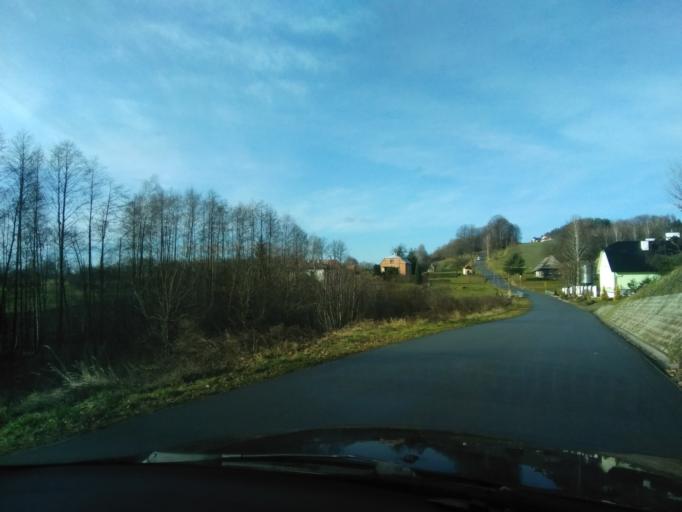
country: PL
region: Subcarpathian Voivodeship
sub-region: Powiat krosnienski
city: Korczyna
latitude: 49.7236
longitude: 21.8024
